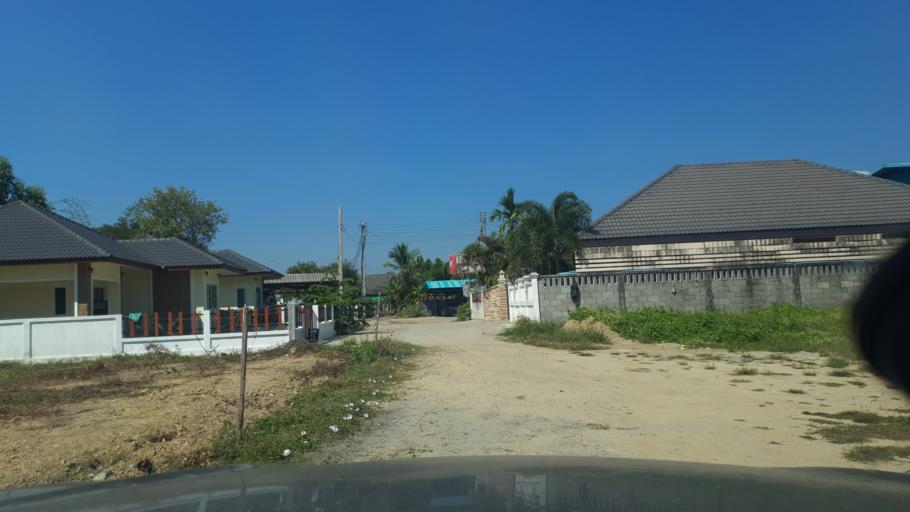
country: TH
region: Chiang Mai
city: San Sai
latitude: 18.8183
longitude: 99.0812
